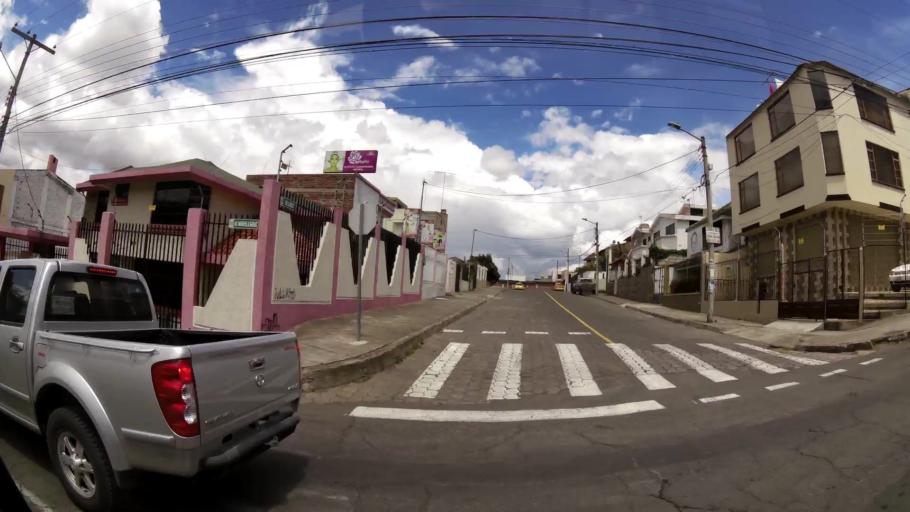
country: EC
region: Tungurahua
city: Ambato
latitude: -1.2644
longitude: -78.6384
